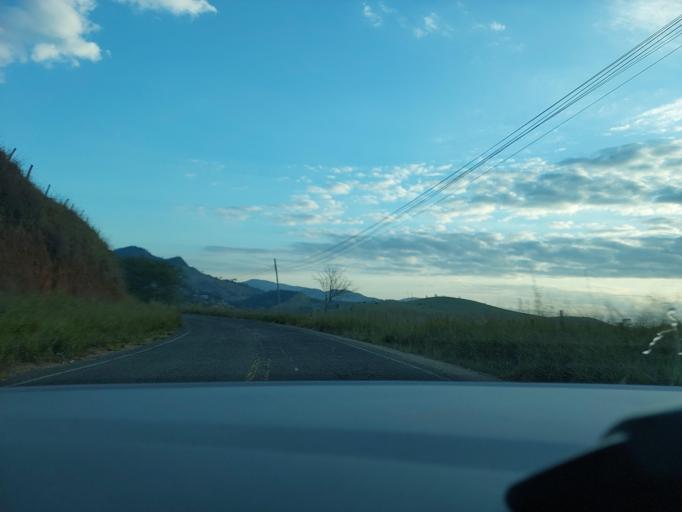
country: BR
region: Rio de Janeiro
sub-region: Natividade
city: Natividade
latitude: -21.1926
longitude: -42.1157
